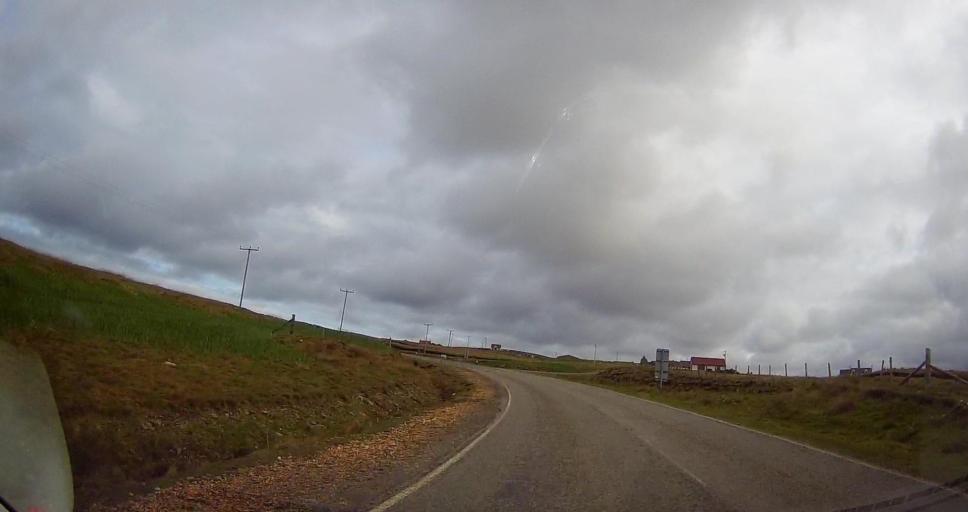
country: GB
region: Scotland
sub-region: Shetland Islands
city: Shetland
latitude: 60.4989
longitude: -1.1576
